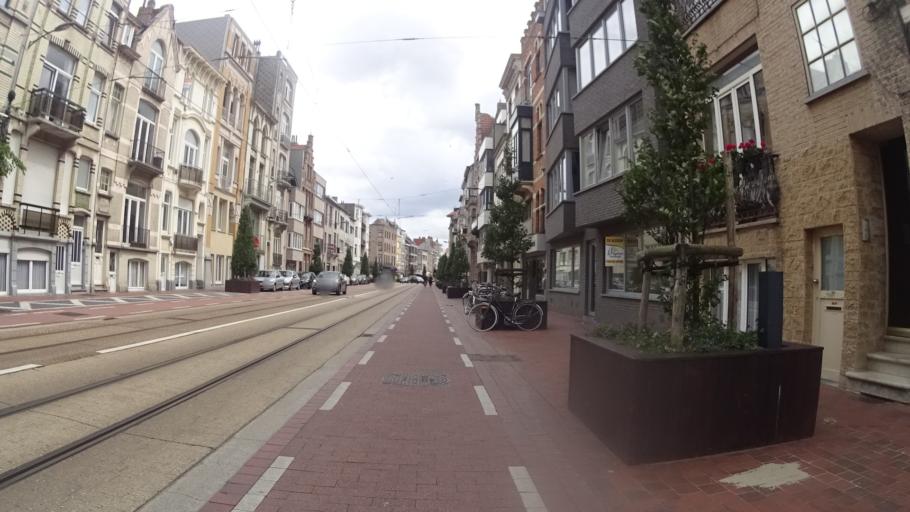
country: BE
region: Flanders
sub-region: Provincie West-Vlaanderen
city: Blankenberge
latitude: 51.3126
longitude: 3.1260
